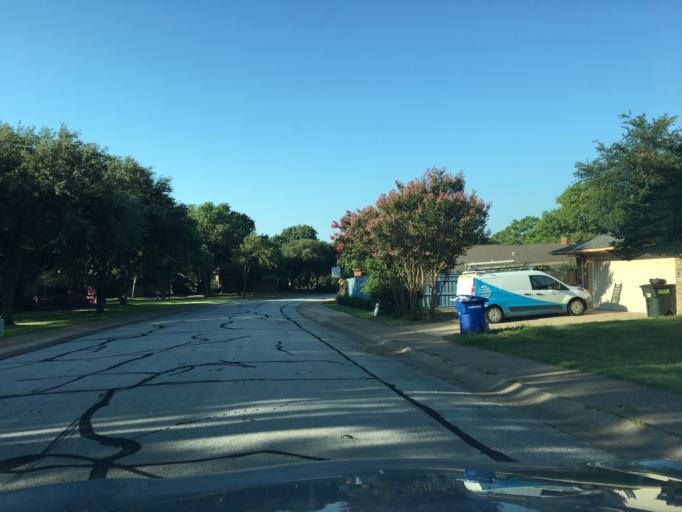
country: US
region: Texas
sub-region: Dallas County
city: Addison
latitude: 32.9659
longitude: -96.8565
